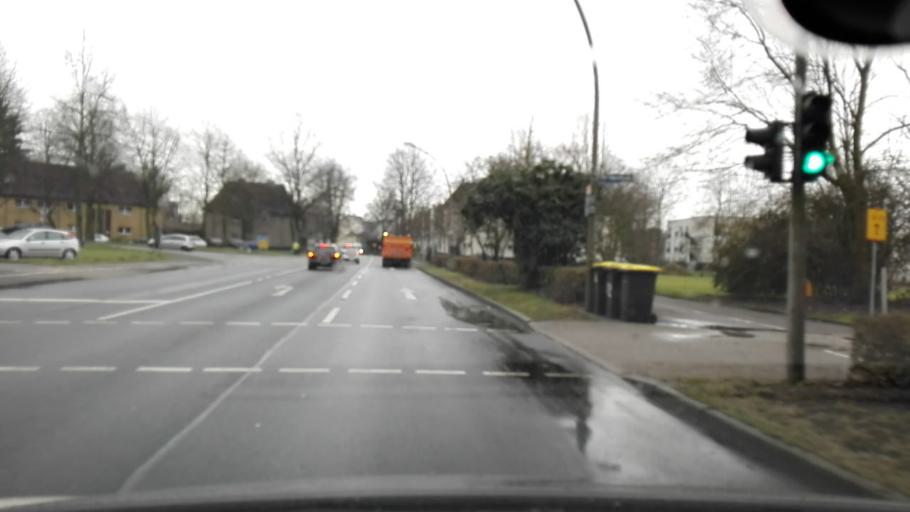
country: DE
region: North Rhine-Westphalia
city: Kamen
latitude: 51.5888
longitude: 7.6586
